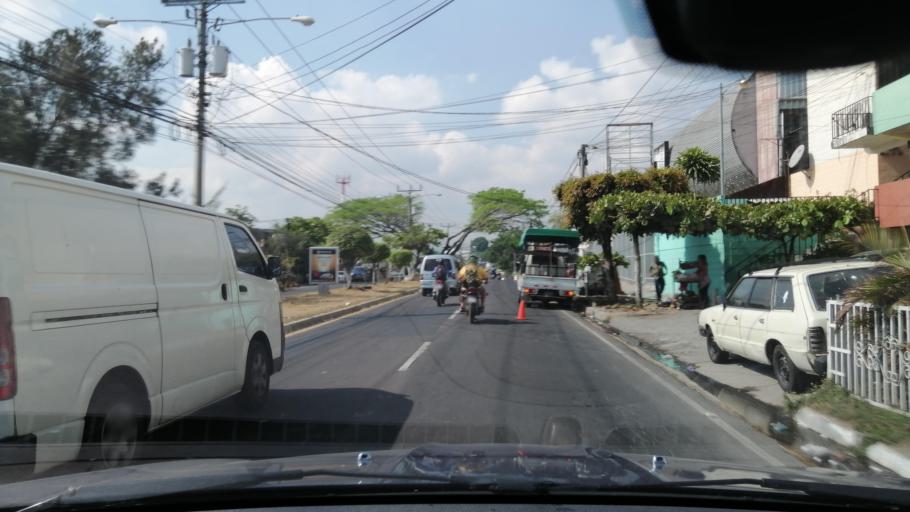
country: SV
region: San Salvador
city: Mejicanos
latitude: 13.7273
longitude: -89.2207
